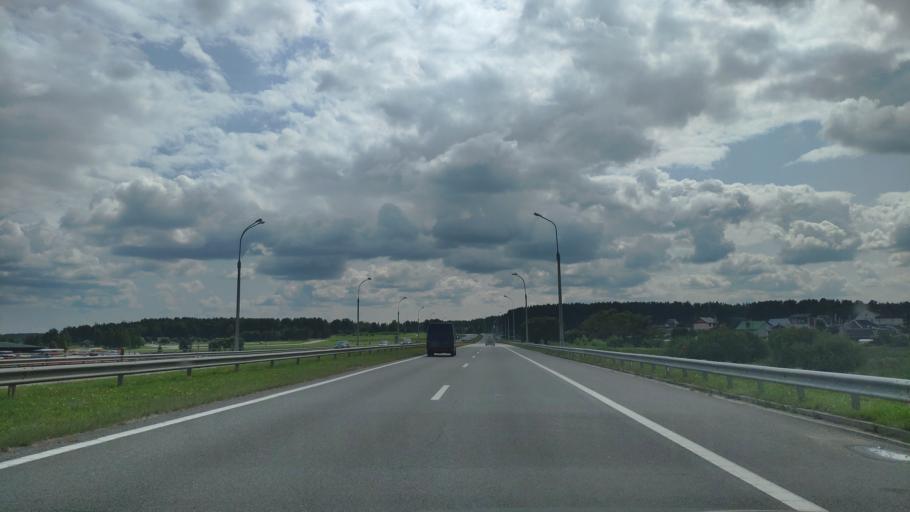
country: BY
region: Minsk
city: Zaslawye
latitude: 54.0003
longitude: 27.3074
